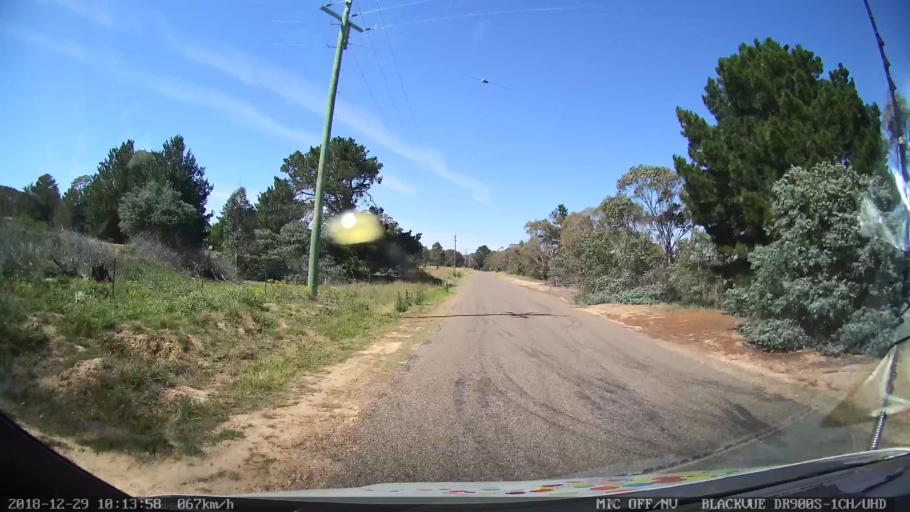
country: AU
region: New South Wales
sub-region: Yass Valley
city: Gundaroo
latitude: -34.9081
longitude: 149.4409
